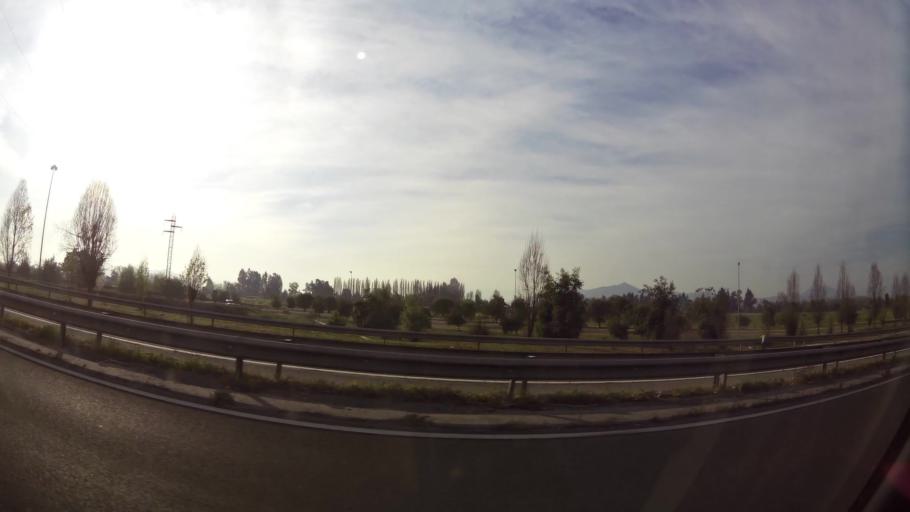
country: CL
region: Santiago Metropolitan
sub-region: Provincia de Talagante
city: Penaflor
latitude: -33.6113
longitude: -70.8529
